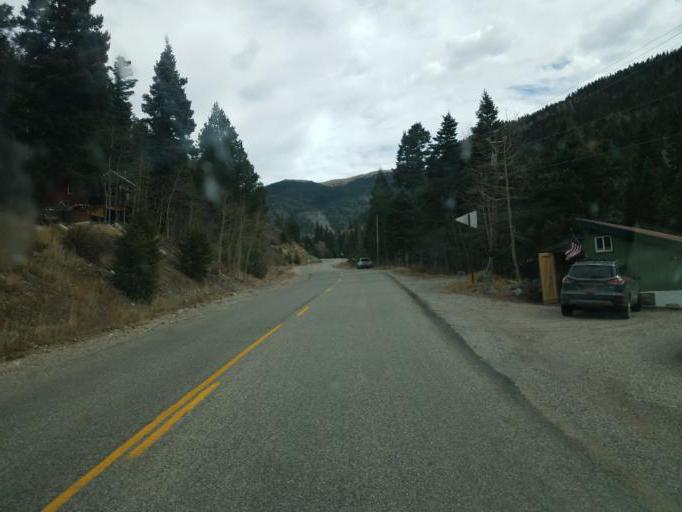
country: US
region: New Mexico
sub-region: Taos County
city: Arroyo Seco
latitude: 36.5954
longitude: -105.4708
